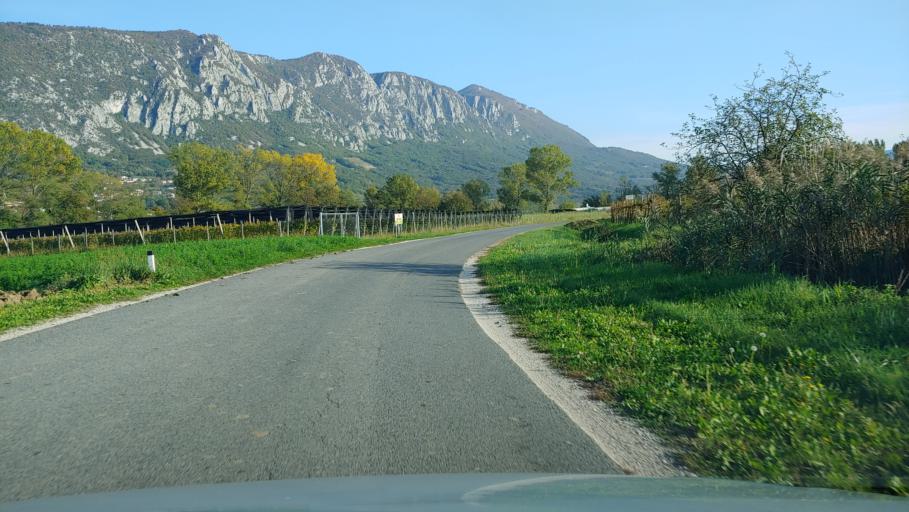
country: SI
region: Vipava
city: Vipava
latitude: 45.8373
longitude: 13.9475
